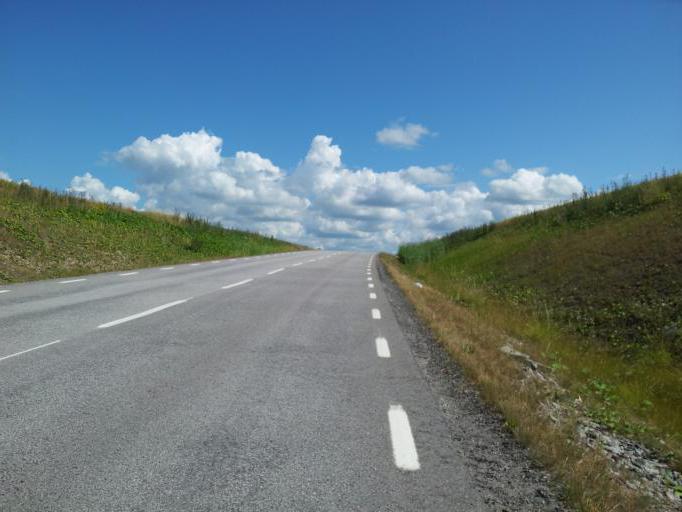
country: SE
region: Uppsala
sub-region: Uppsala Kommun
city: Saevja
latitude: 59.8769
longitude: 17.6966
